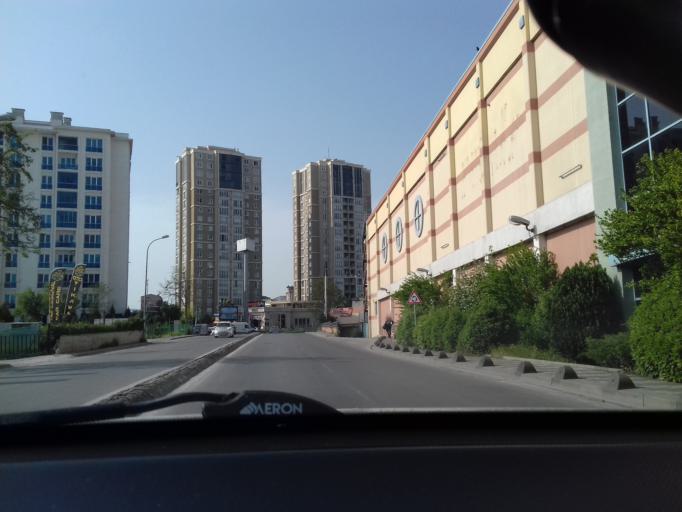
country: TR
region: Istanbul
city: Maltepe
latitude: 40.9120
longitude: 29.2106
